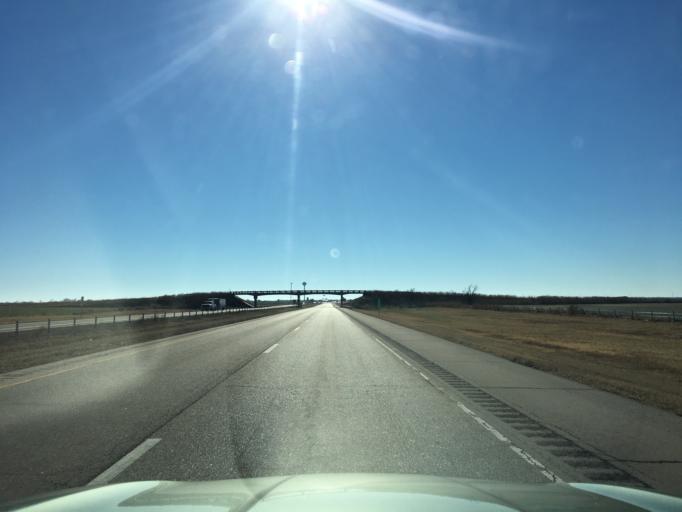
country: US
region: Oklahoma
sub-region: Kay County
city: Blackwell
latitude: 36.9582
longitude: -97.3458
